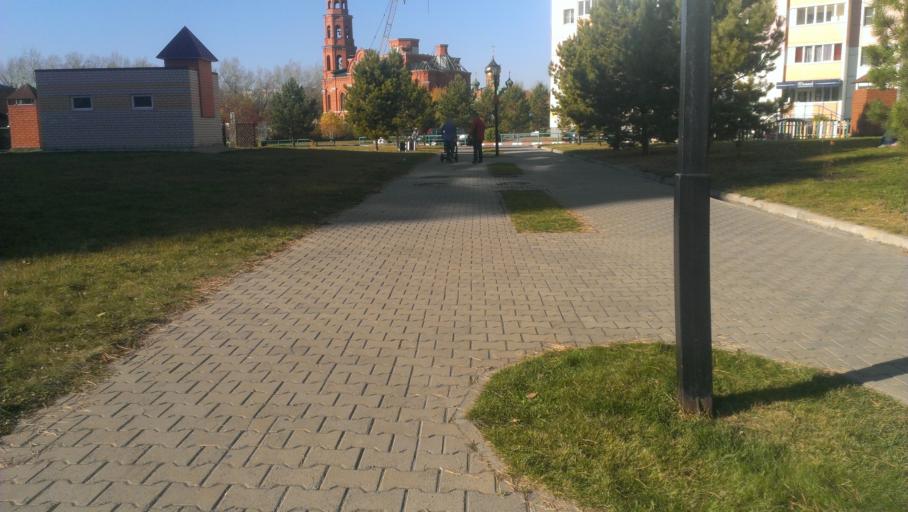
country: RU
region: Altai Krai
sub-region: Gorod Barnaulskiy
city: Barnaul
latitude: 53.3581
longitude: 83.6920
